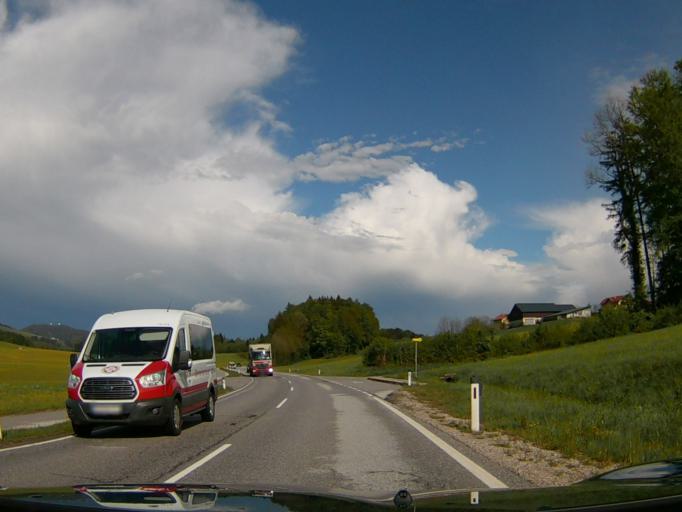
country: AT
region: Salzburg
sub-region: Politischer Bezirk Salzburg-Umgebung
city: Plainfeld
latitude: 47.8544
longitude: 13.1859
